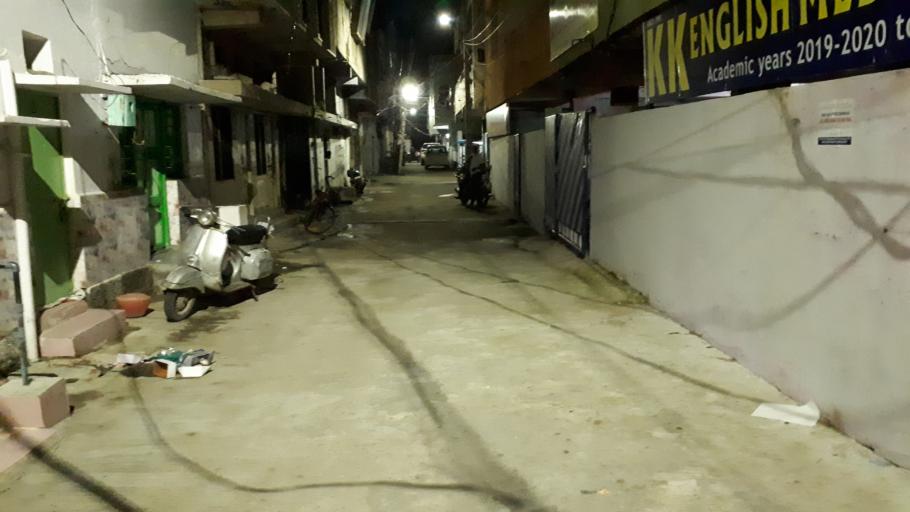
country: IN
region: Telangana
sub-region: Karimnagar
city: Karimnagar
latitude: 18.4354
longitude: 79.1259
